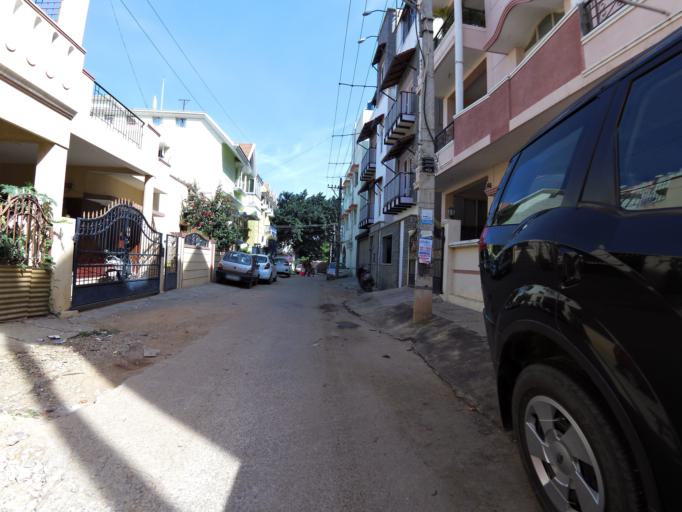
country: IN
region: Karnataka
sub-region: Bangalore Urban
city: Bangalore
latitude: 13.0032
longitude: 77.6337
